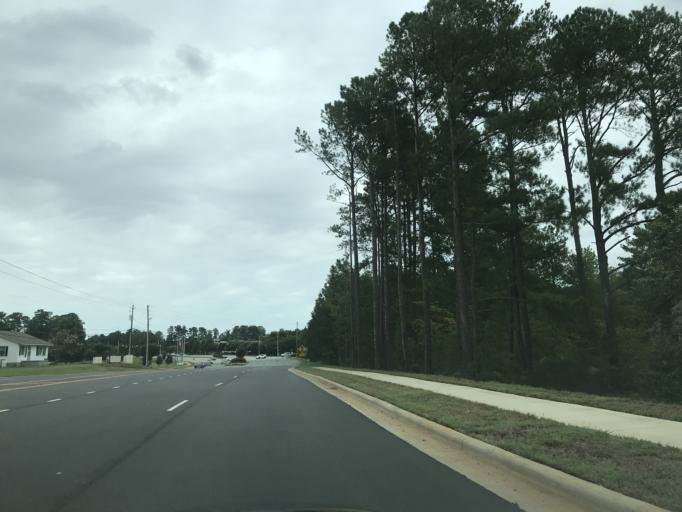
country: US
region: North Carolina
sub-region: Wake County
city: Cary
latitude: 35.7421
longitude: -78.7419
